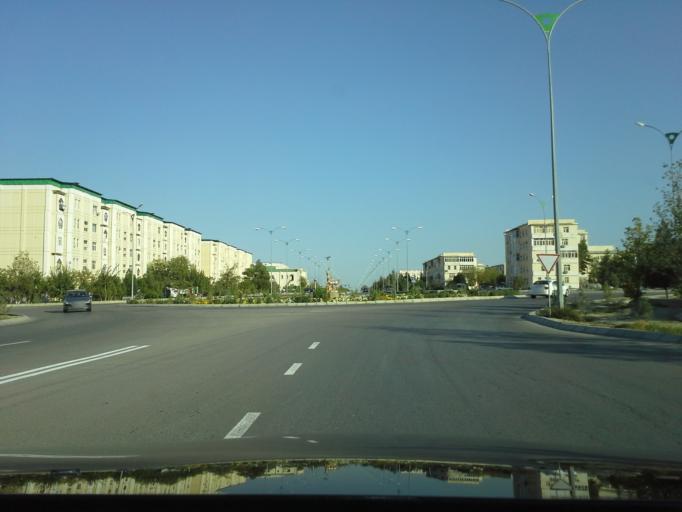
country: TM
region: Ahal
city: Abadan
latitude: 38.0553
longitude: 58.1485
